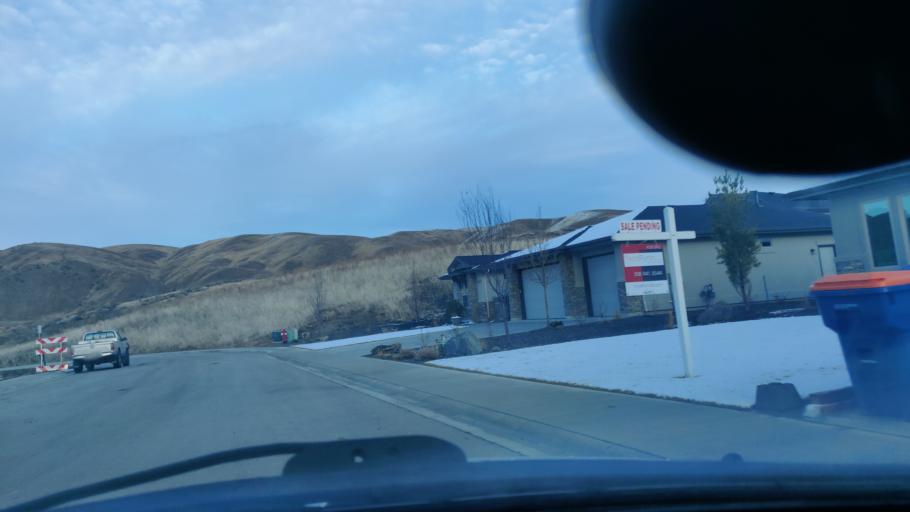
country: US
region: Idaho
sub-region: Ada County
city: Eagle
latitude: 43.7760
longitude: -116.2589
